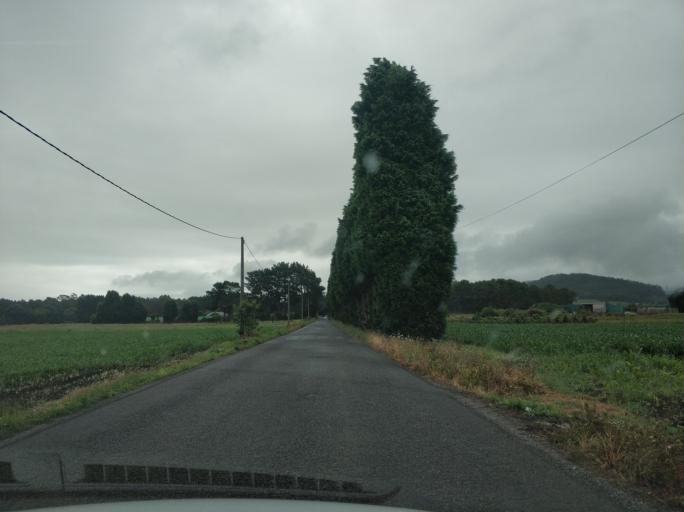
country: ES
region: Asturias
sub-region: Province of Asturias
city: Tineo
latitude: 43.5527
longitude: -6.4574
